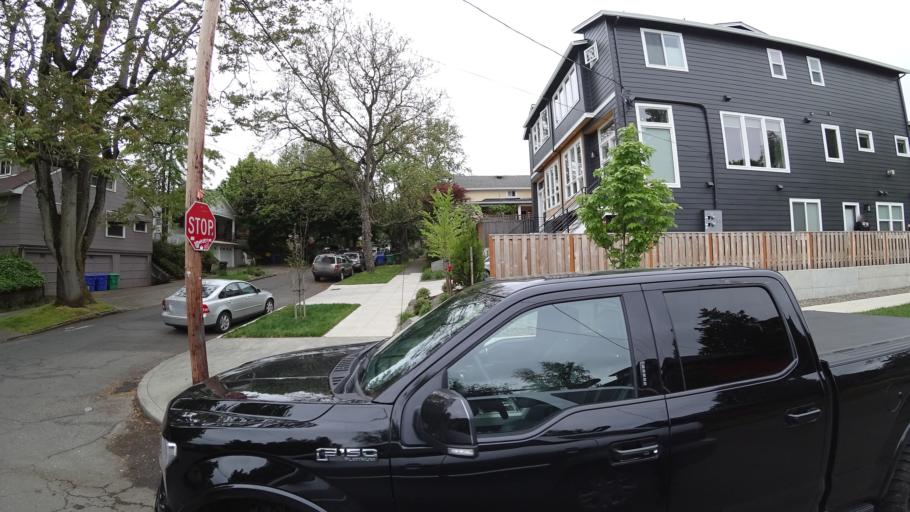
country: US
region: Oregon
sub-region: Multnomah County
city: Portland
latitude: 45.5171
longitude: -122.6380
